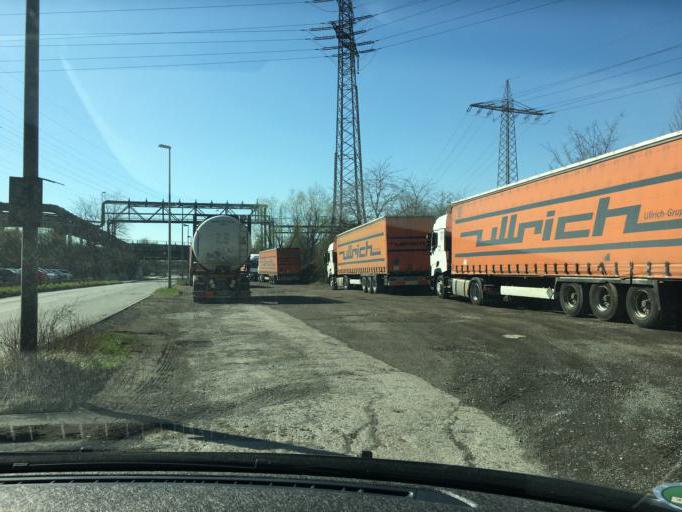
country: DE
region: North Rhine-Westphalia
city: Meiderich
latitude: 51.4888
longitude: 6.7255
